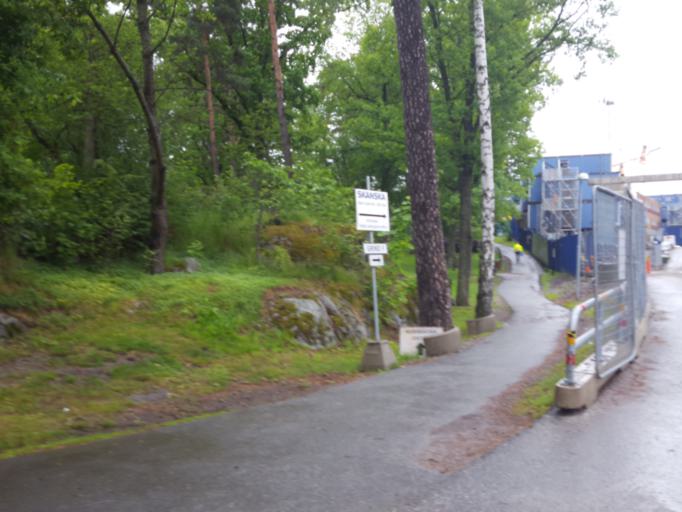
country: SE
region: Stockholm
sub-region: Norrtalje Kommun
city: Bergshamra
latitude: 59.3509
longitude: 18.0315
